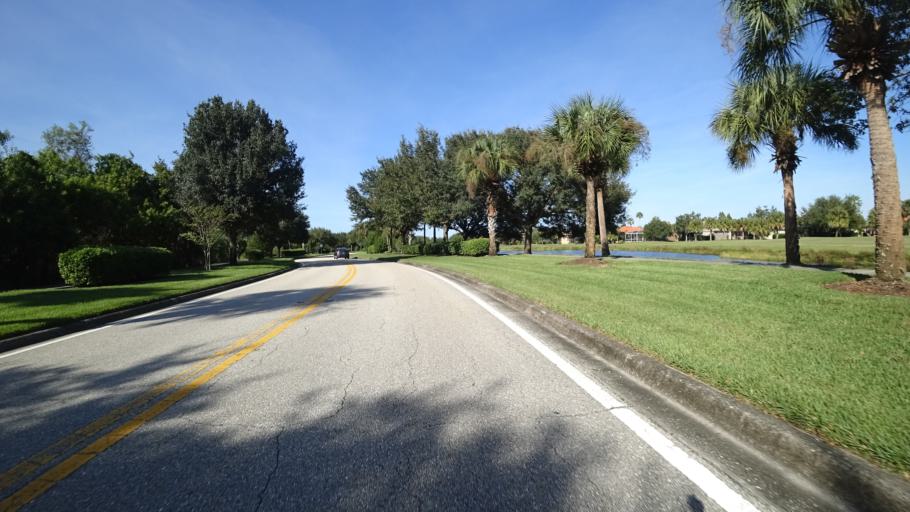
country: US
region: Florida
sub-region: Sarasota County
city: Desoto Lakes
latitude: 27.4256
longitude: -82.4677
